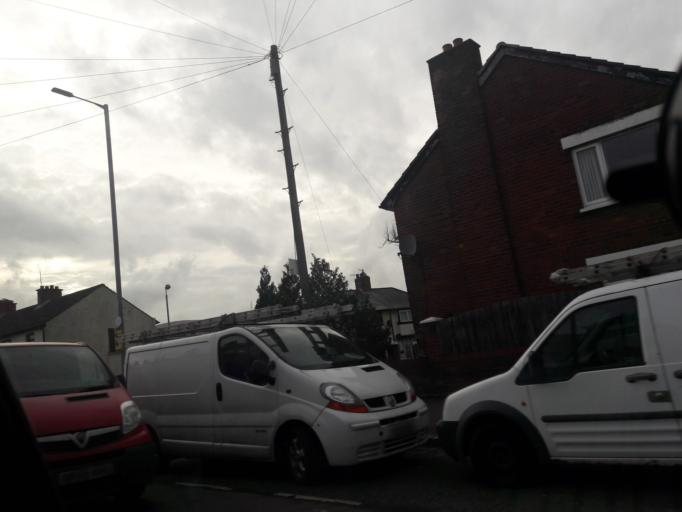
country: GB
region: Northern Ireland
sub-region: City of Belfast
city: Belfast
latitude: 54.6183
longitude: -5.9539
